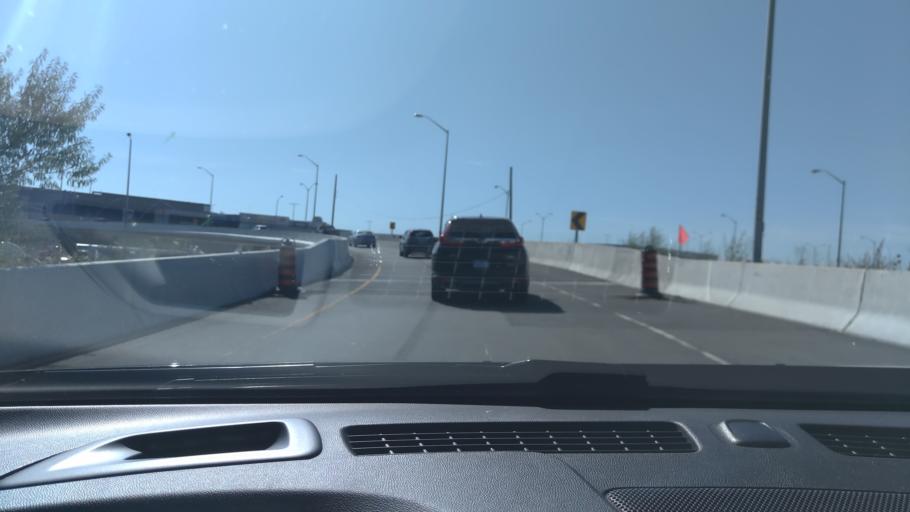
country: CA
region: Ontario
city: Toronto
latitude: 43.7303
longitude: -79.4515
